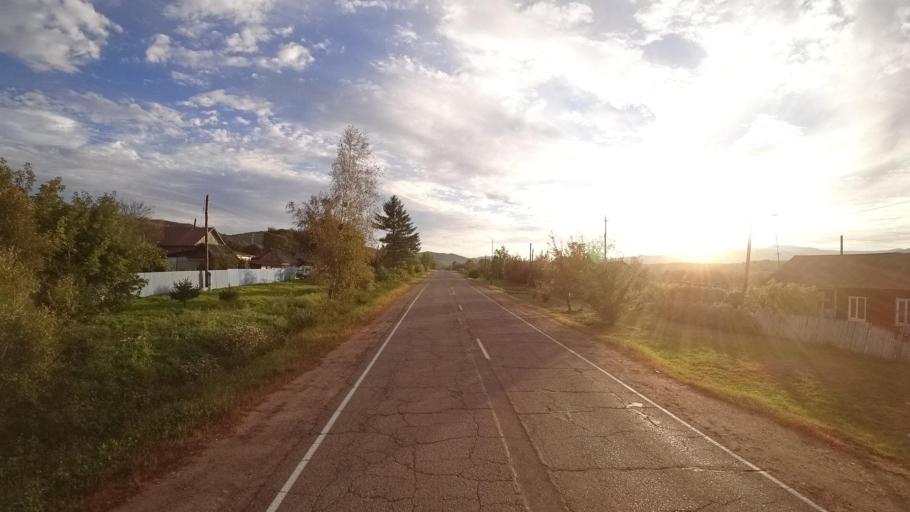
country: RU
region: Primorskiy
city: Yakovlevka
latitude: 44.4196
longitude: 133.4555
